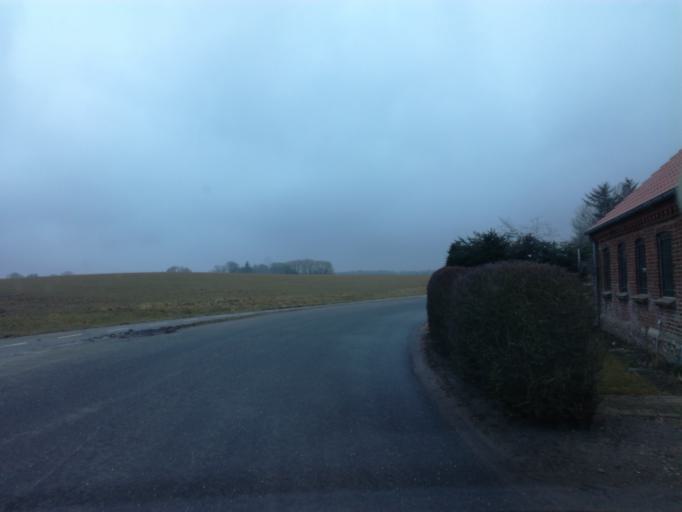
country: DK
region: South Denmark
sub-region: Vejle Kommune
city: Borkop
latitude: 55.6292
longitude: 9.5899
